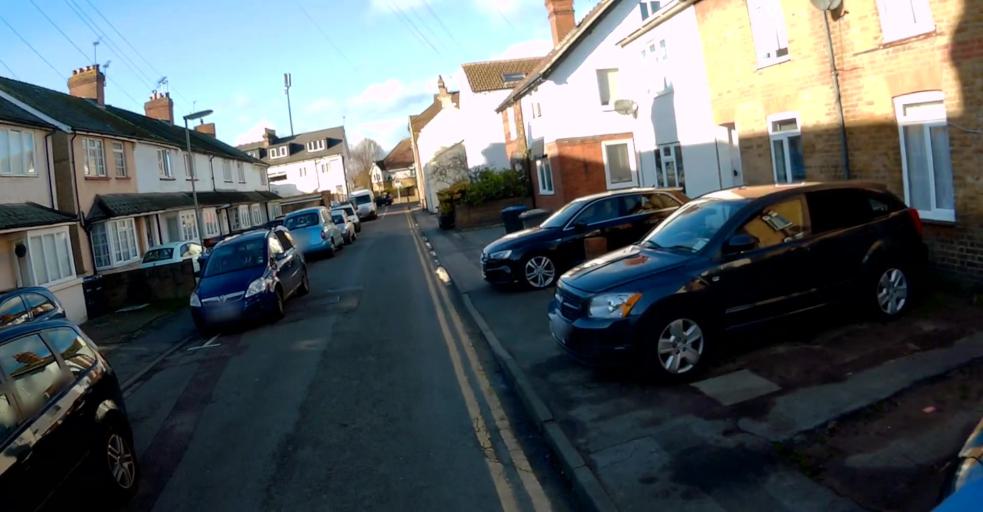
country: GB
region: England
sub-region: Surrey
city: Addlestone
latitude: 51.3726
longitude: -0.4827
